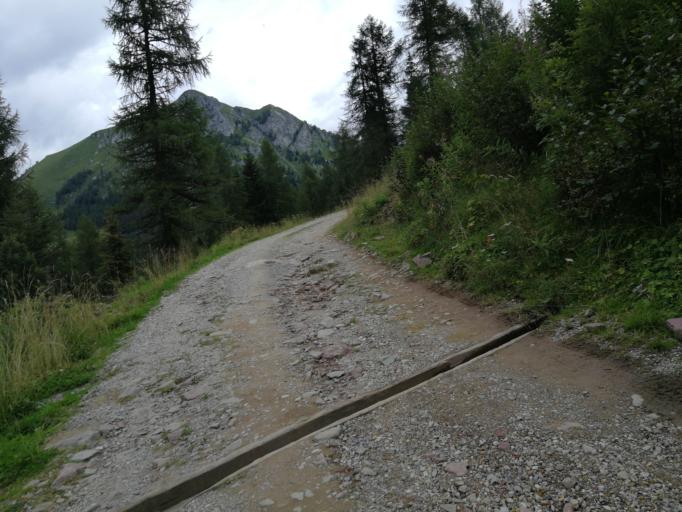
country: IT
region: Trentino-Alto Adige
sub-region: Provincia di Trento
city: Brione
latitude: 45.9370
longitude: 10.5346
